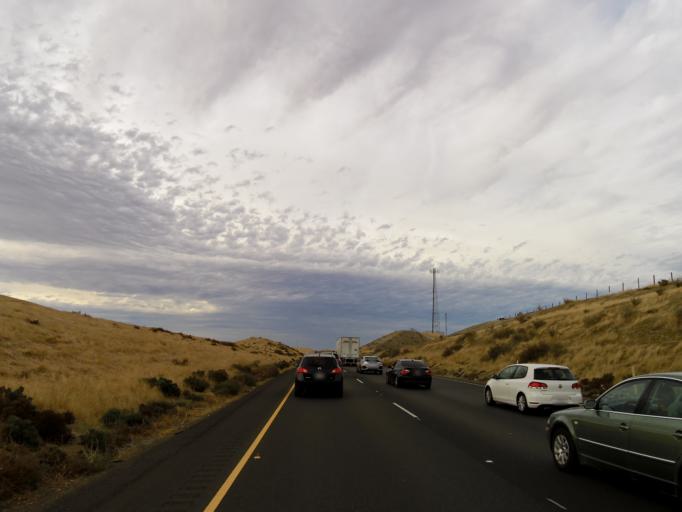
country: US
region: California
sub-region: Kings County
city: Kettleman City
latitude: 35.9866
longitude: -119.9649
